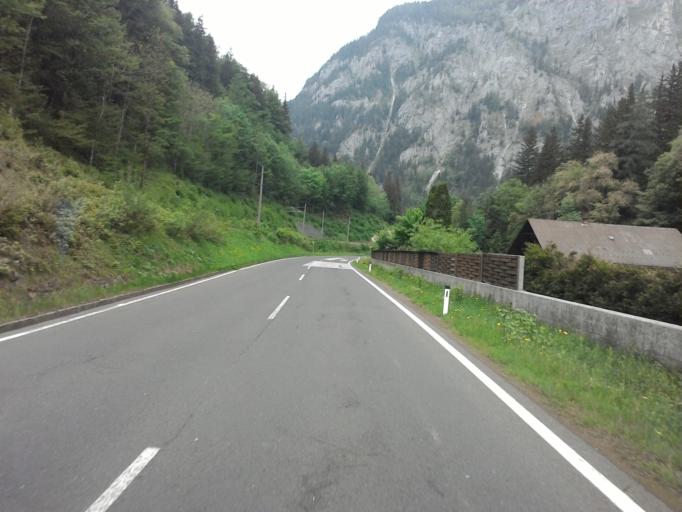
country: AT
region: Styria
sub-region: Politischer Bezirk Leoben
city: Eisenerz
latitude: 47.5692
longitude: 14.8507
